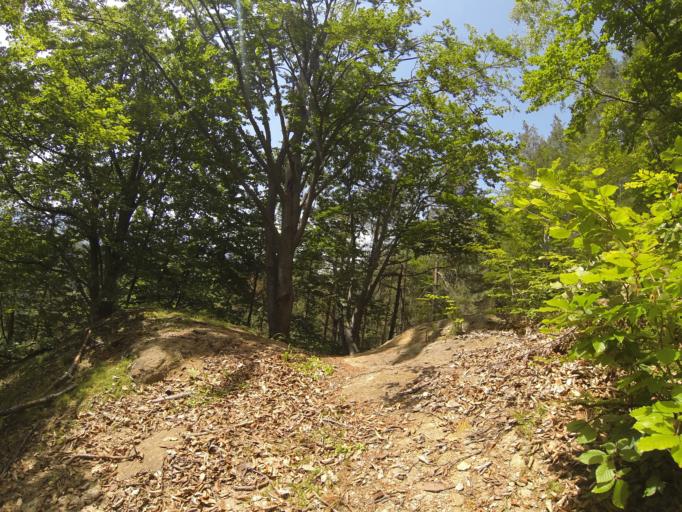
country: RO
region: Valcea
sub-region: Oras Baile Olanesti
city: Cheia
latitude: 45.2241
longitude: 24.1894
